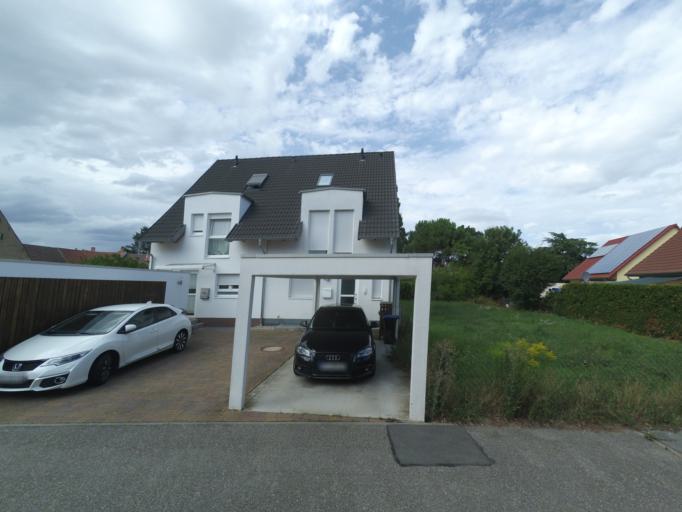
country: DE
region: Rheinland-Pfalz
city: Schifferstadt
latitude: 49.3841
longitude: 8.3642
